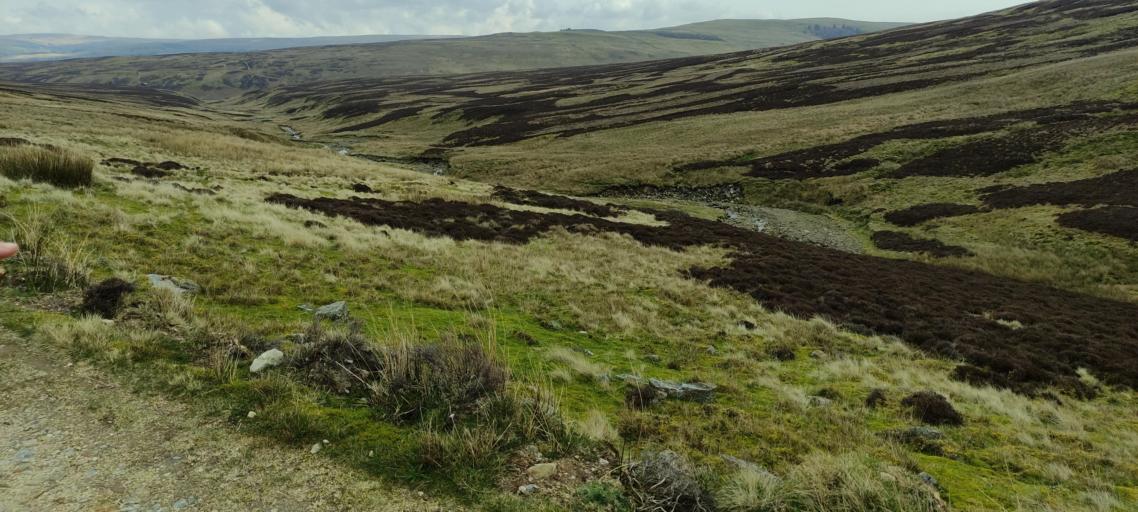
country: GB
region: England
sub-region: Cumbria
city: Appleby-in-Westmorland
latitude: 54.7464
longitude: -2.5085
